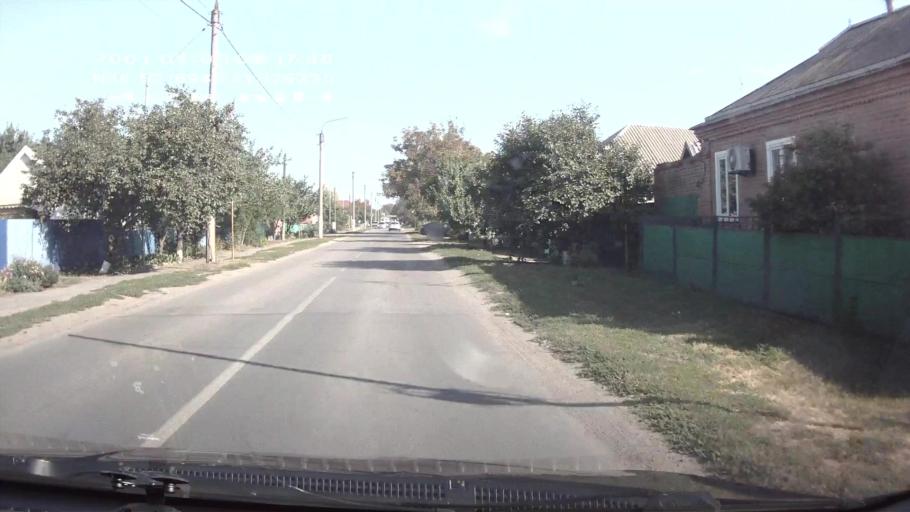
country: RU
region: Rostov
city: Tselina
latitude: 46.5318
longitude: 41.0262
